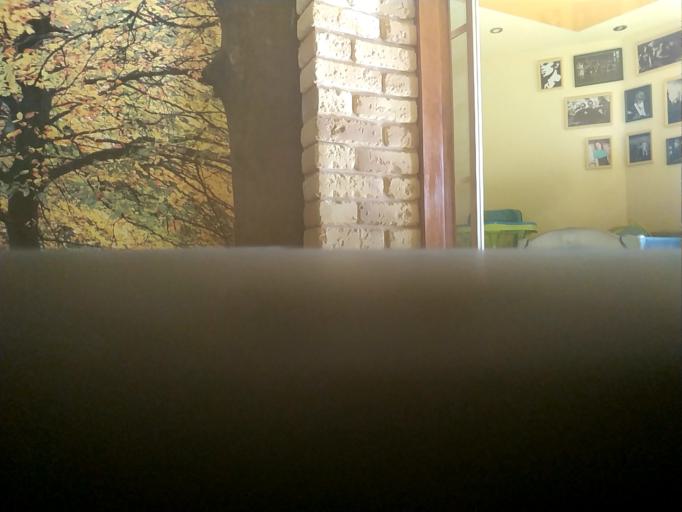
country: RU
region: Smolensk
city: Temkino
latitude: 55.0049
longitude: 34.9358
